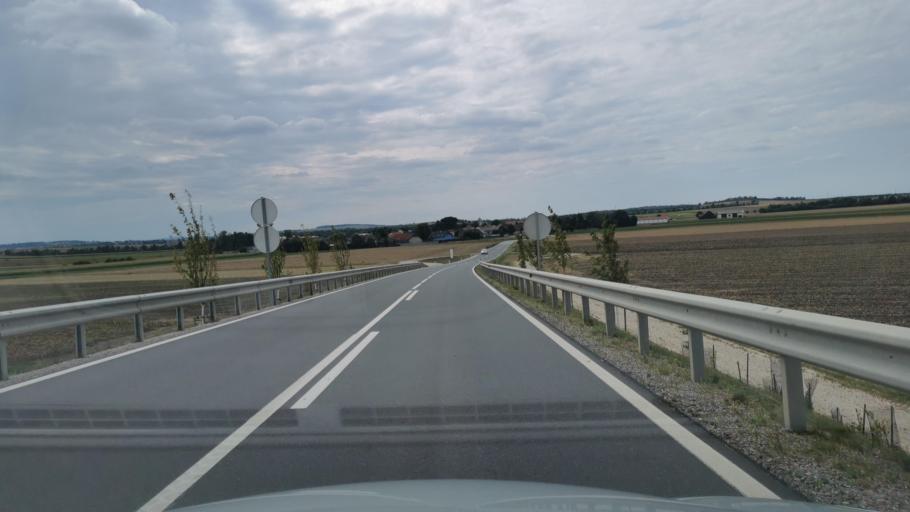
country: AT
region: Lower Austria
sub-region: Politischer Bezirk Hollabrunn
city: Wullersdorf
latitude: 48.6297
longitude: 16.0763
